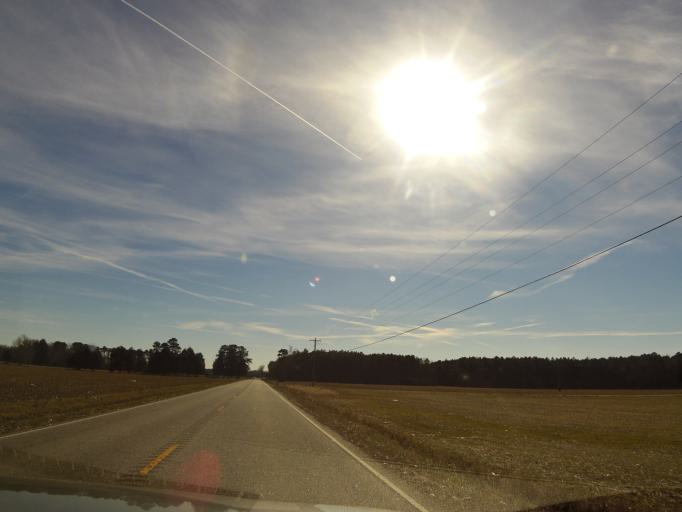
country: US
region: Virginia
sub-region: Isle of Wight County
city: Isle of Wight
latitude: 36.9377
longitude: -76.6871
